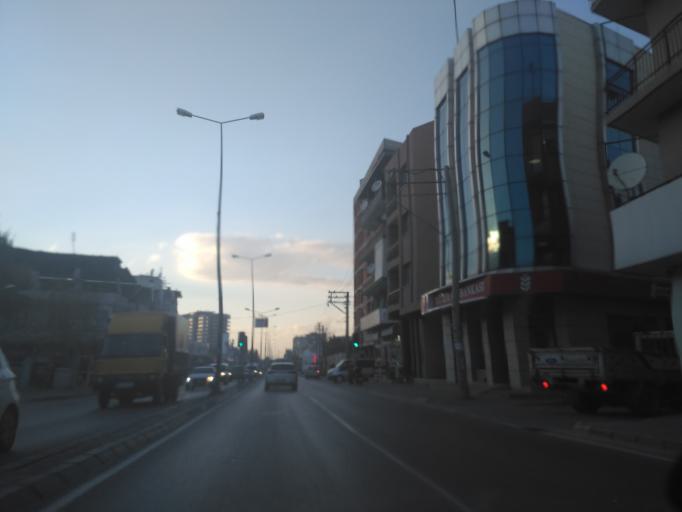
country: TR
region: Izmir
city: Buca
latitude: 38.4301
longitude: 27.2003
